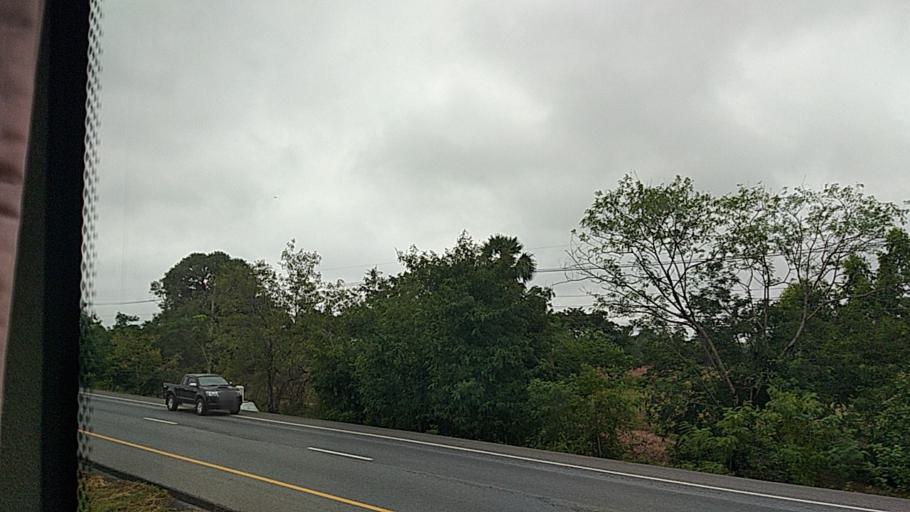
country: TH
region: Nakhon Ratchasima
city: Non Daeng
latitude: 15.4027
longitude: 102.4740
